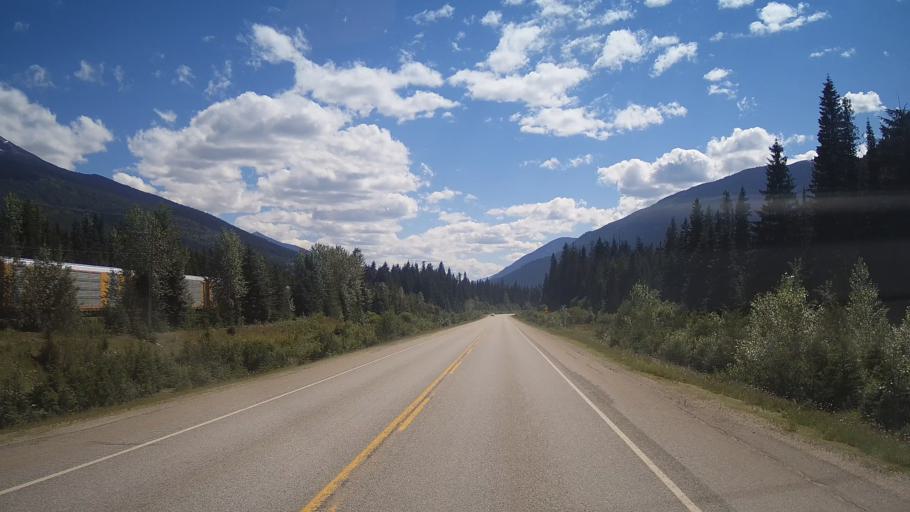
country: CA
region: Alberta
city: Jasper Park Lodge
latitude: 52.5745
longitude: -119.0987
